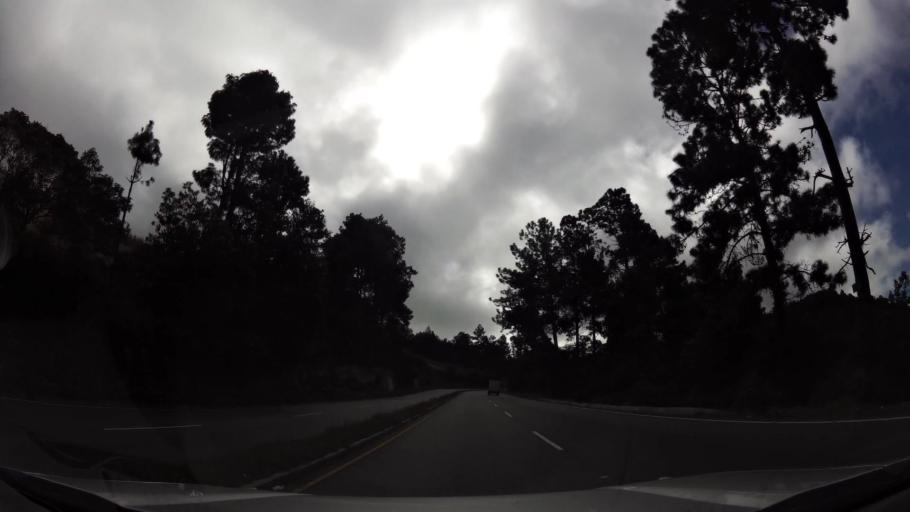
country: GT
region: Quetzaltenango
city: Salcaja
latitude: 14.8608
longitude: -91.4079
